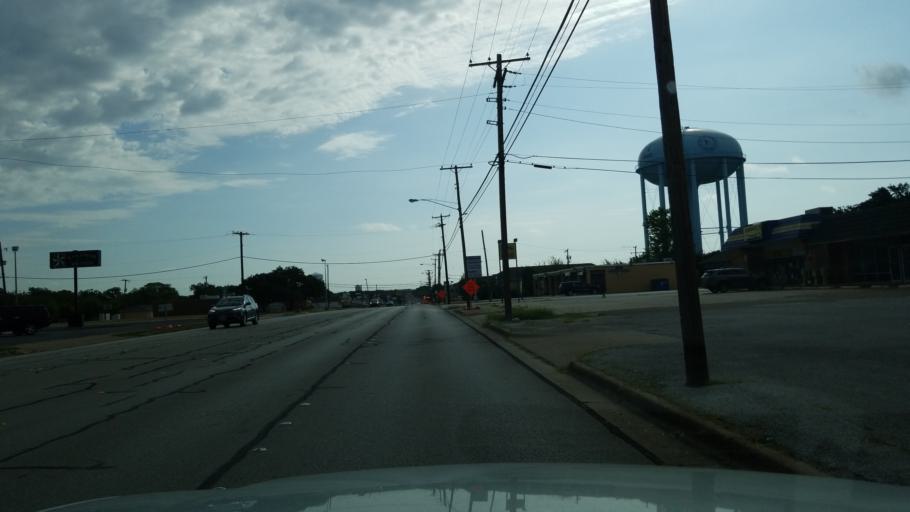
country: US
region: Texas
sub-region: Tarrant County
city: Hurst
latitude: 32.8339
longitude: -97.1748
